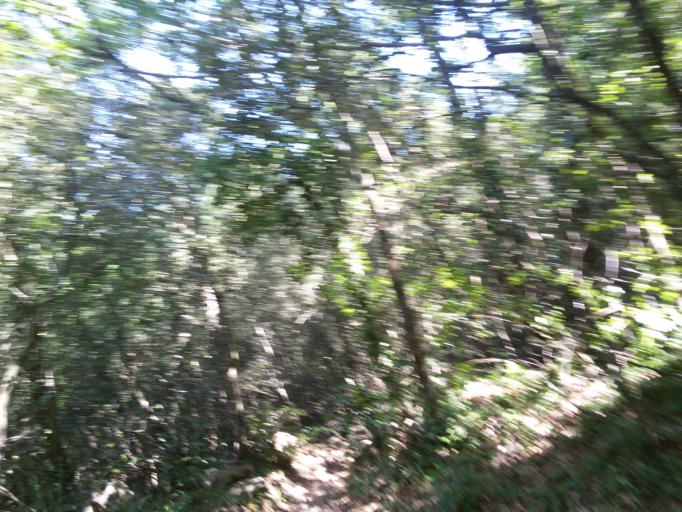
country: IT
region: Liguria
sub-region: Provincia di Savona
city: Borgio
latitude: 44.1704
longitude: 8.3179
